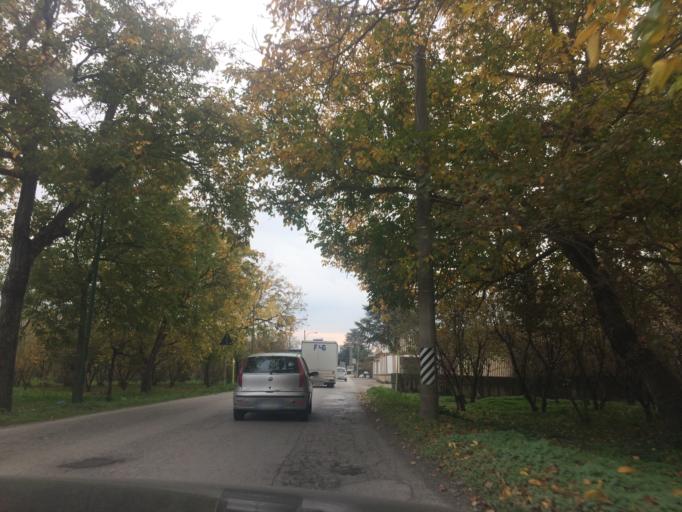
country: IT
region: Campania
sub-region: Provincia di Napoli
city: Piazzolla
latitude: 40.8841
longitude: 14.5300
